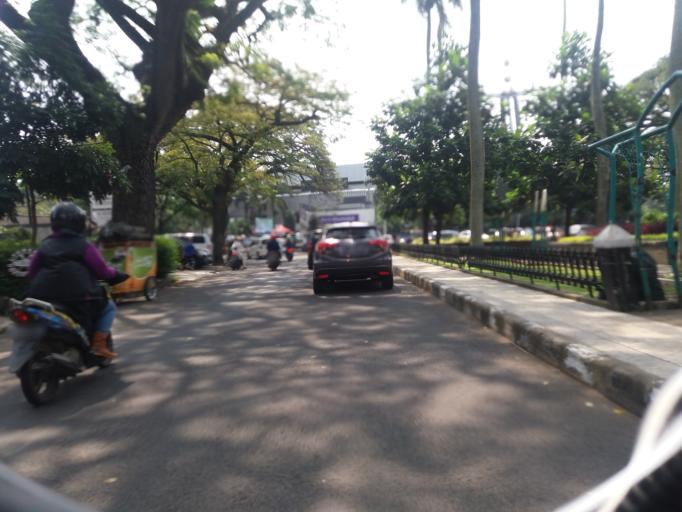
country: ID
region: West Java
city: Bandung
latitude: -6.9056
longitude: 107.6214
